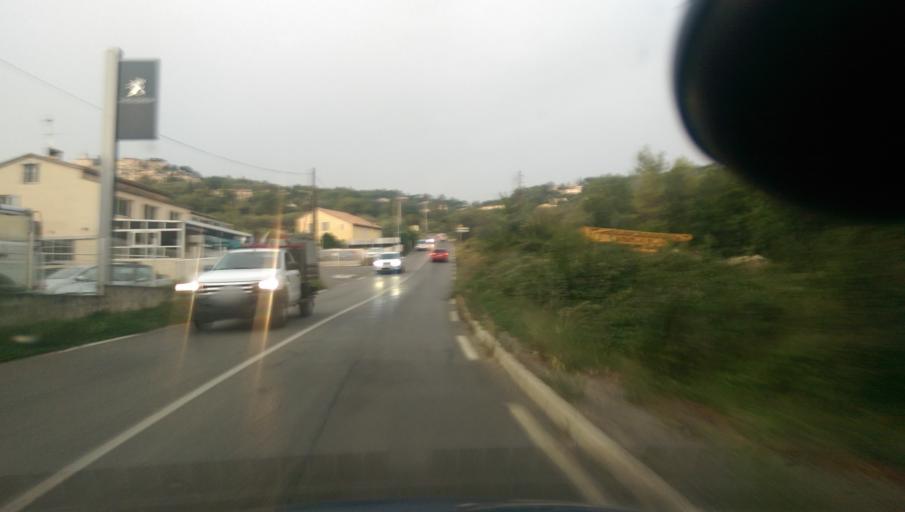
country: FR
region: Provence-Alpes-Cote d'Azur
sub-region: Departement des Alpes-Maritimes
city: Opio
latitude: 43.6700
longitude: 6.9840
